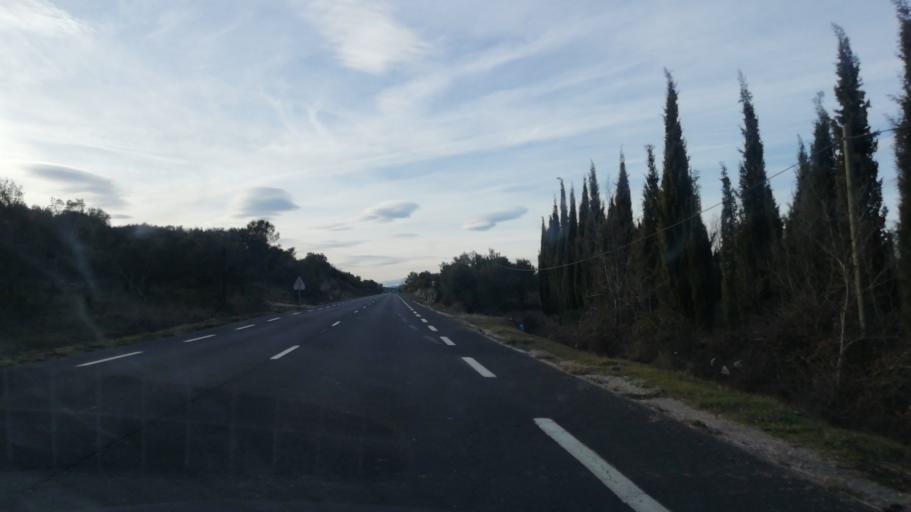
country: FR
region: Languedoc-Roussillon
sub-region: Departement du Gard
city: Clarensac
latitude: 43.8572
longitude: 4.2387
